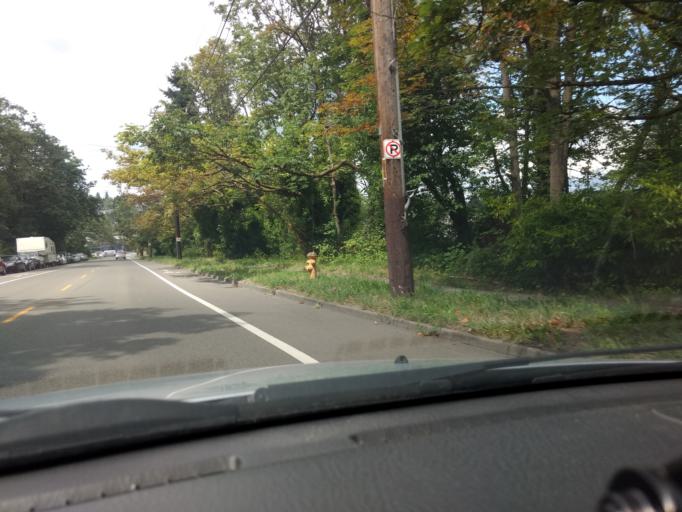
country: US
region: Washington
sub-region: King County
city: Riverton
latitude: 47.5216
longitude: -122.2744
